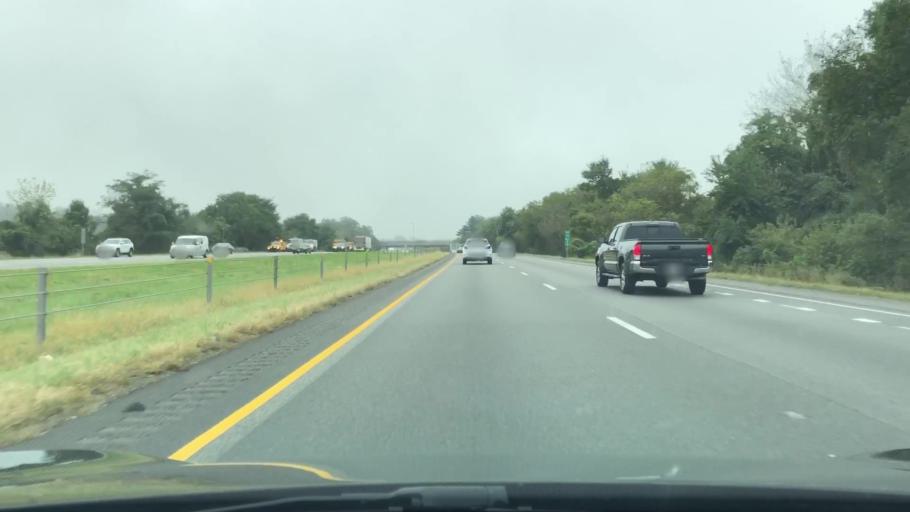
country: US
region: Pennsylvania
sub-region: Bucks County
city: Woodside
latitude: 40.2298
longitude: -74.8822
